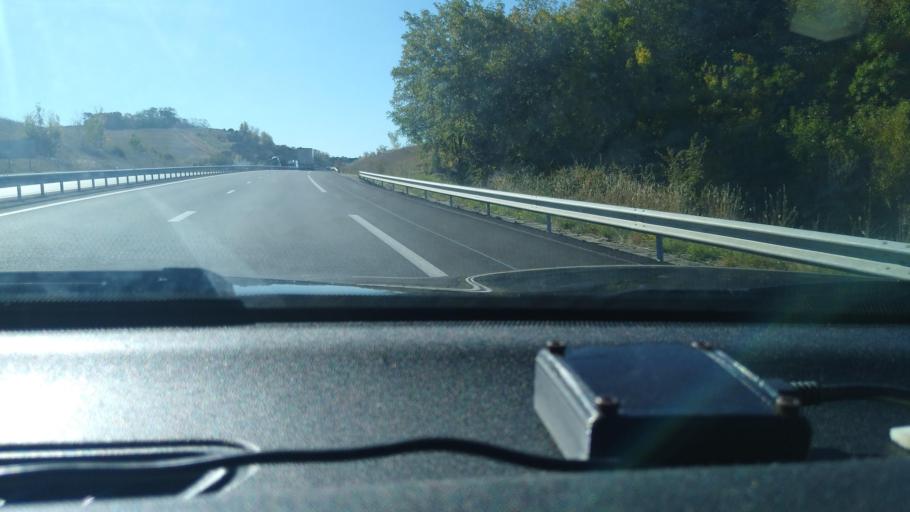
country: FR
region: Midi-Pyrenees
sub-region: Departement de l'Ariege
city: Mazeres
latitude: 43.2833
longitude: 1.6748
